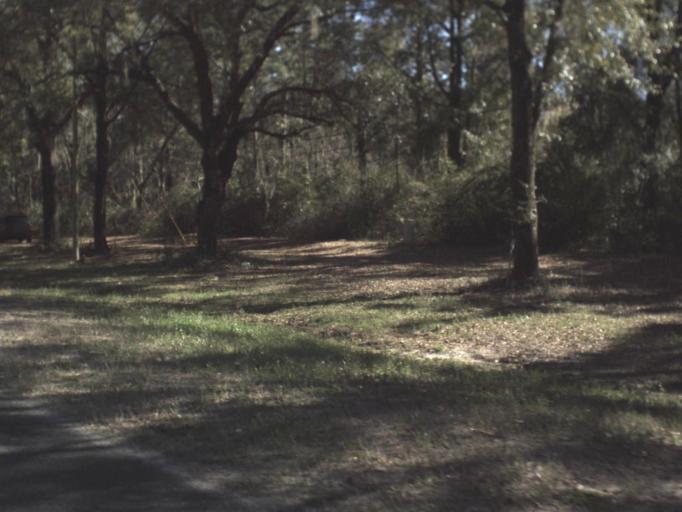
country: US
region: Florida
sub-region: Gadsden County
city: Midway
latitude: 30.4654
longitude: -84.3969
